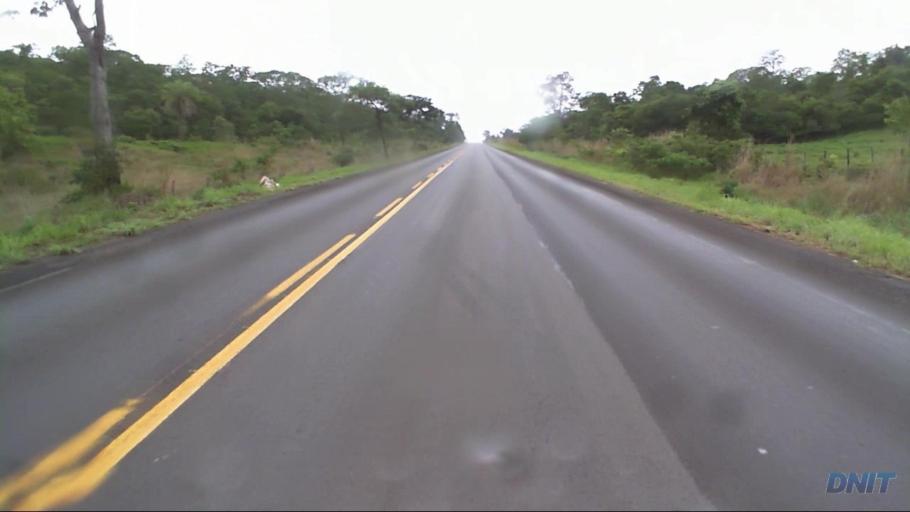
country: BR
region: Goias
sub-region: Padre Bernardo
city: Padre Bernardo
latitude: -15.2054
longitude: -48.4627
